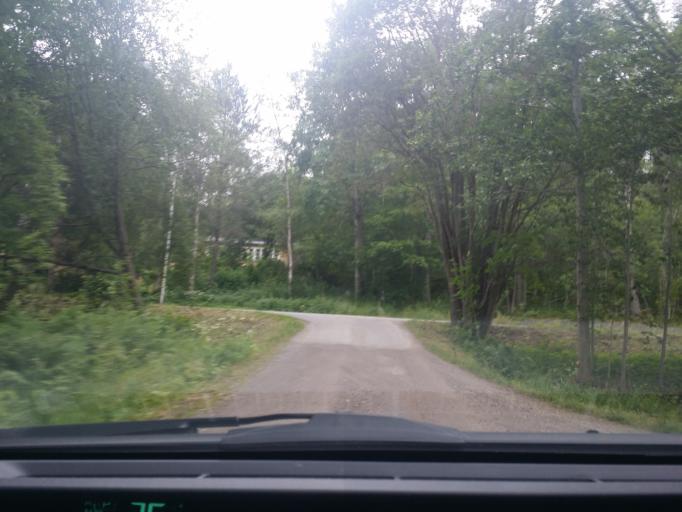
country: SE
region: OErebro
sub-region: Nora Kommun
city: Nora
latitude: 59.5339
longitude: 15.0336
